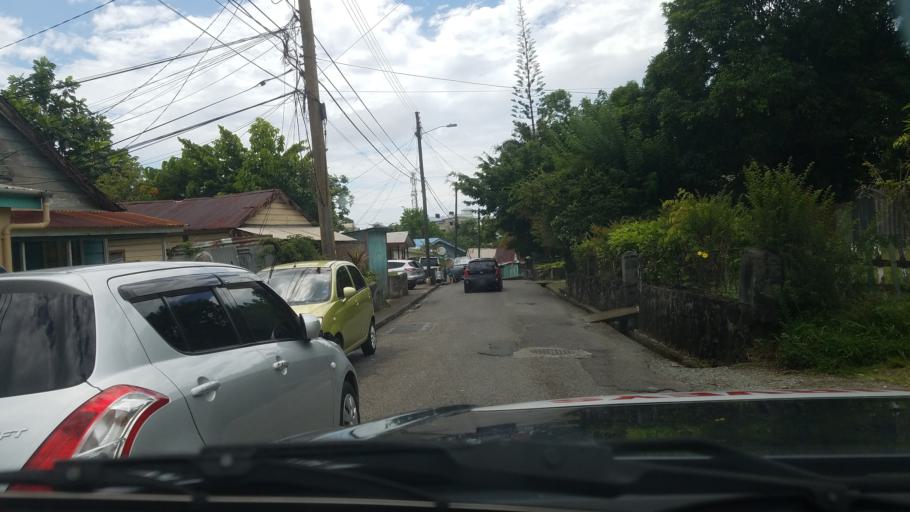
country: LC
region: Castries Quarter
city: Bisee
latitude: 14.0054
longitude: -60.9840
